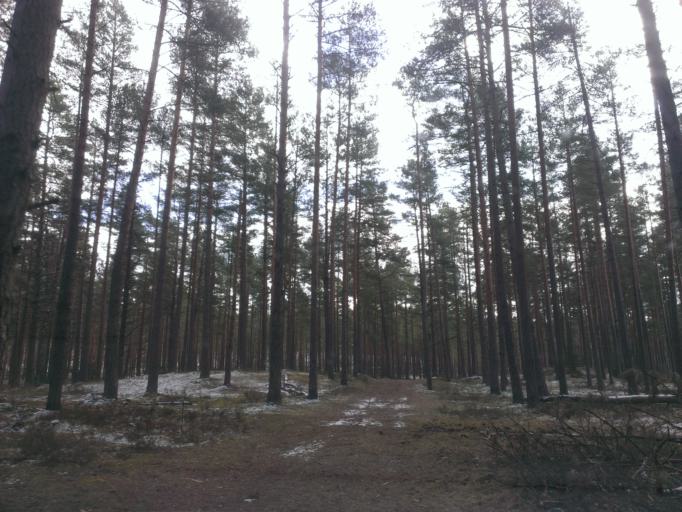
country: LV
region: Garkalne
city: Garkalne
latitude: 56.9656
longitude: 24.4327
